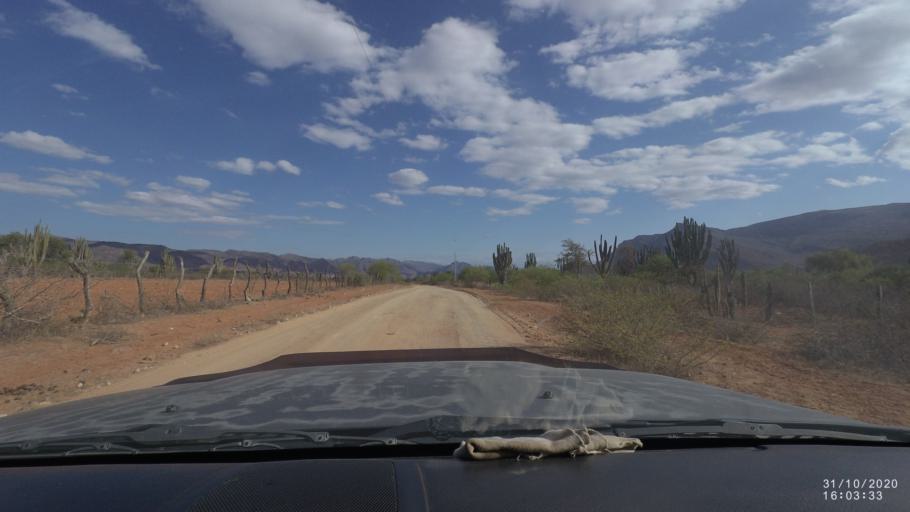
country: BO
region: Chuquisaca
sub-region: Provincia Zudanez
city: Mojocoya
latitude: -18.3527
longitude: -64.6525
